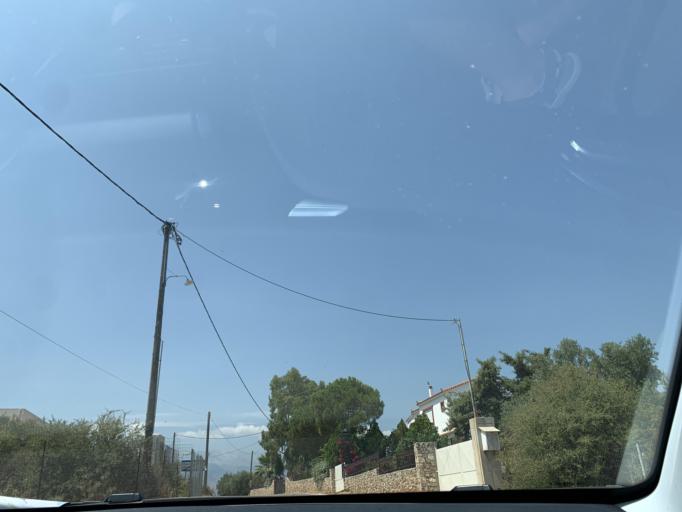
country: GR
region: Crete
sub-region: Nomos Chanias
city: Kalivai
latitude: 35.4504
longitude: 24.2239
